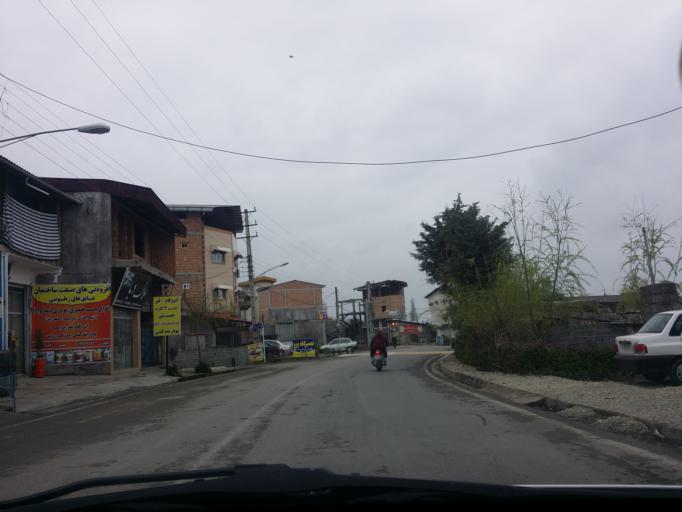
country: IR
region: Mazandaran
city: Chalus
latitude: 36.6651
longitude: 51.3903
